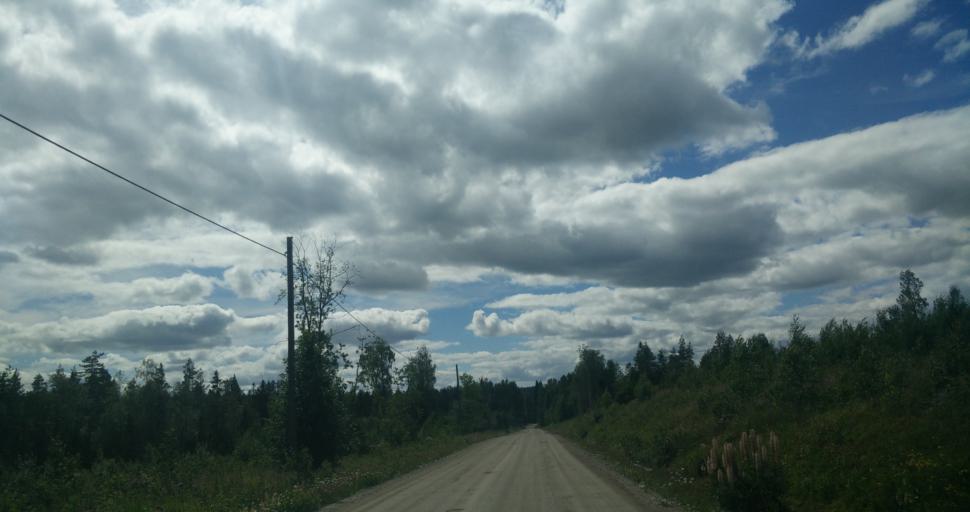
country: SE
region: Gaevleborg
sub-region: Nordanstigs Kommun
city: Bergsjoe
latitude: 62.1324
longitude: 17.1303
